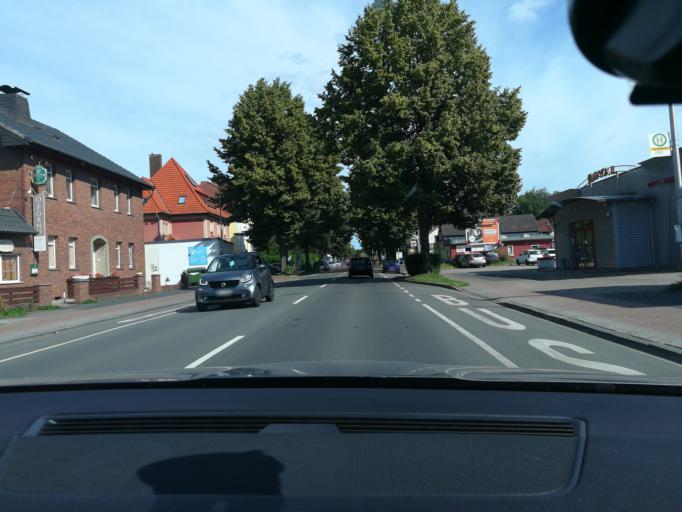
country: DE
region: North Rhine-Westphalia
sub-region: Regierungsbezirk Detmold
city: Minden
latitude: 52.3032
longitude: 8.9054
